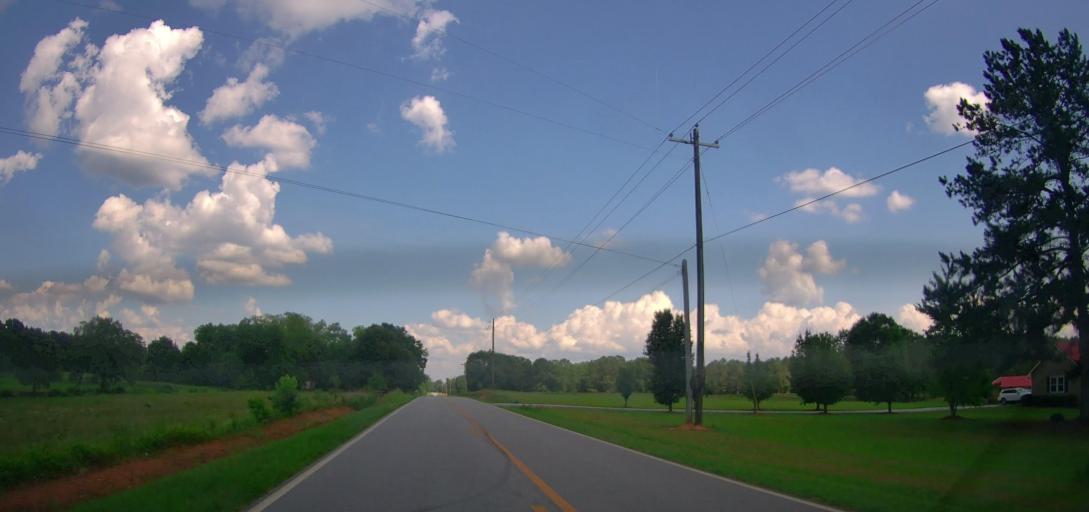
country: US
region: Georgia
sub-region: Butts County
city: Jackson
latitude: 33.2149
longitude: -84.0731
